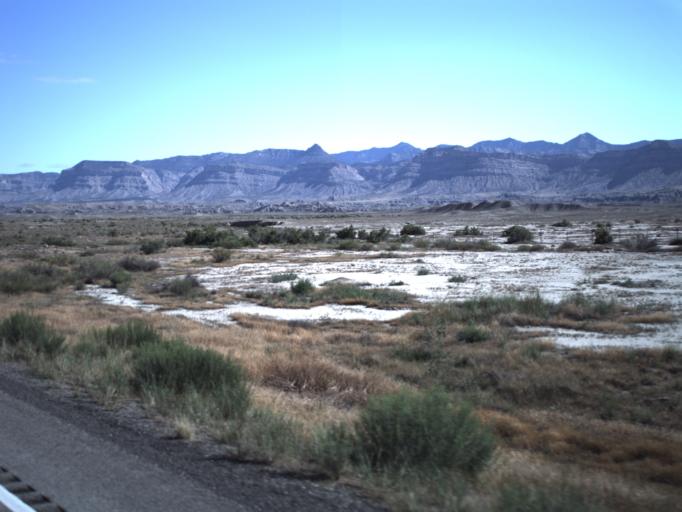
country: US
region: Utah
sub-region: Carbon County
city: East Carbon City
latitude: 39.3292
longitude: -110.3680
